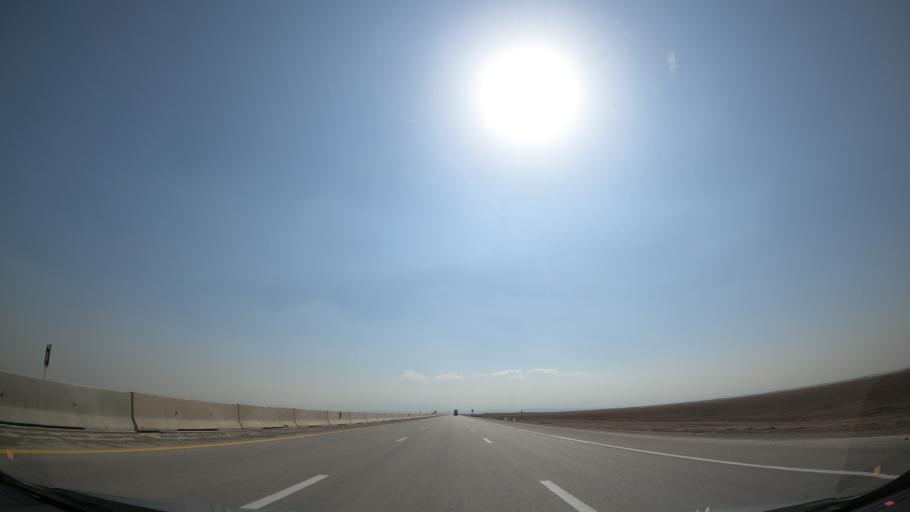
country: IR
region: Qazvin
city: Abyek
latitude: 35.9457
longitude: 50.4676
